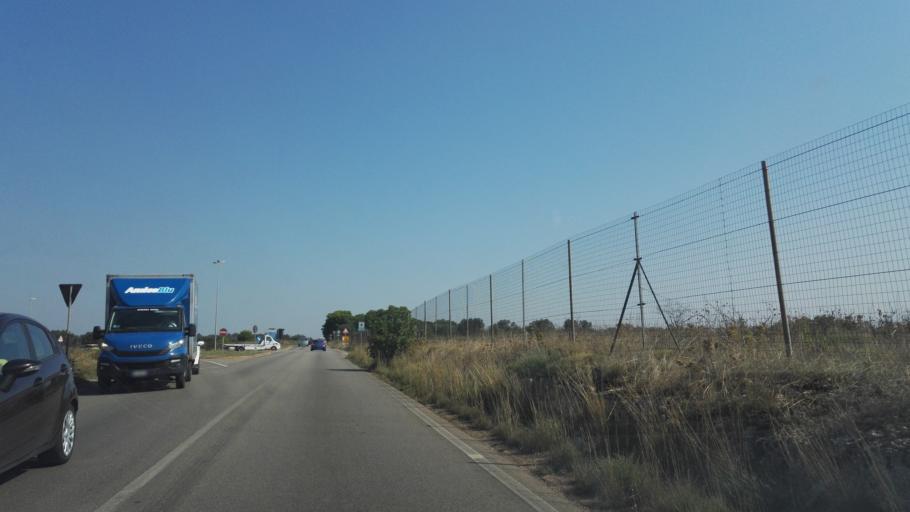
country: IT
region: Apulia
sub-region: Provincia di Lecce
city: Nardo
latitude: 40.1362
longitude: 18.0190
